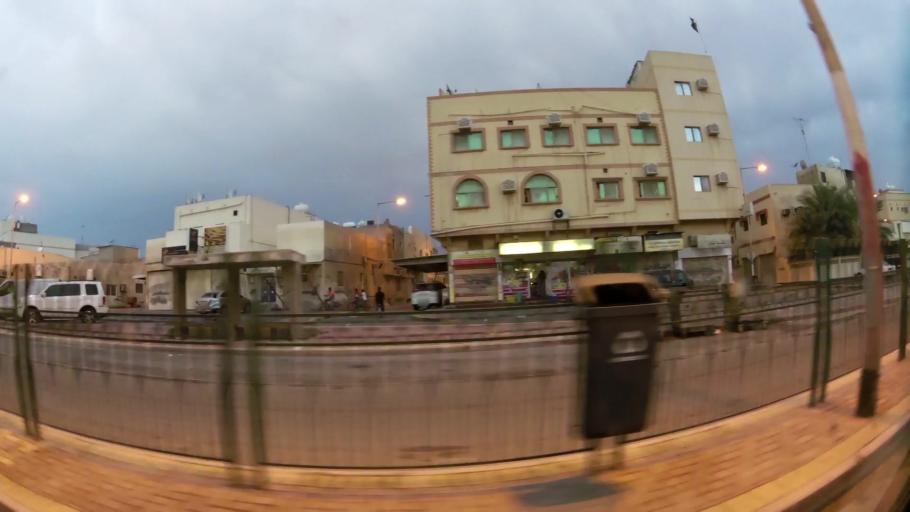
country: BH
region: Northern
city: Madinat `Isa
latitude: 26.1573
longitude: 50.5136
